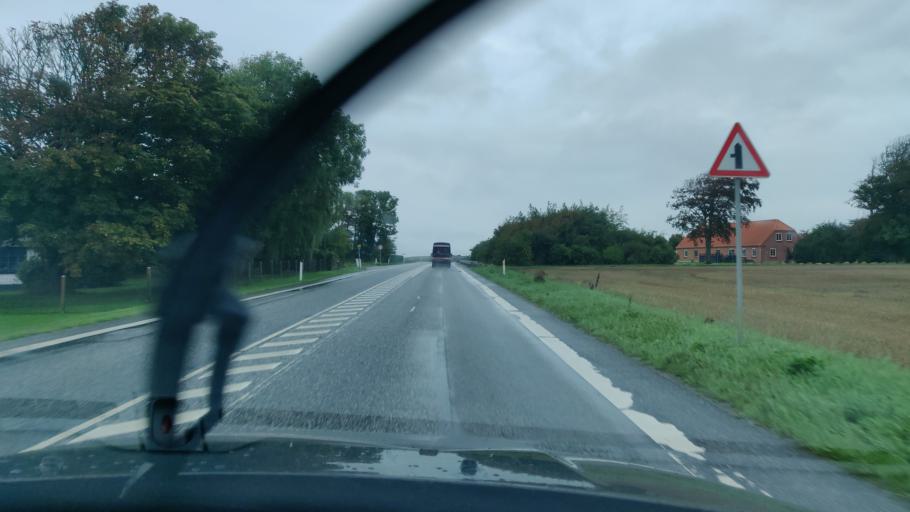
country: DK
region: North Denmark
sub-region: Thisted Kommune
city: Thisted
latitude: 56.9870
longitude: 8.7703
